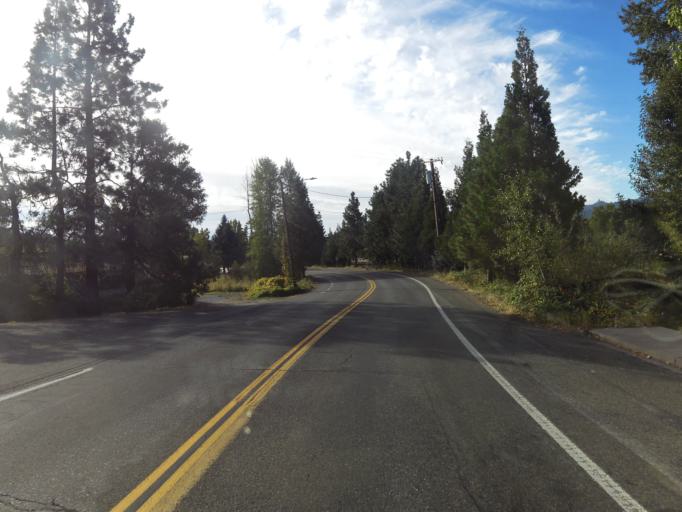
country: US
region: California
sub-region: Siskiyou County
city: Mount Shasta
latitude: 41.3185
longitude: -122.3182
